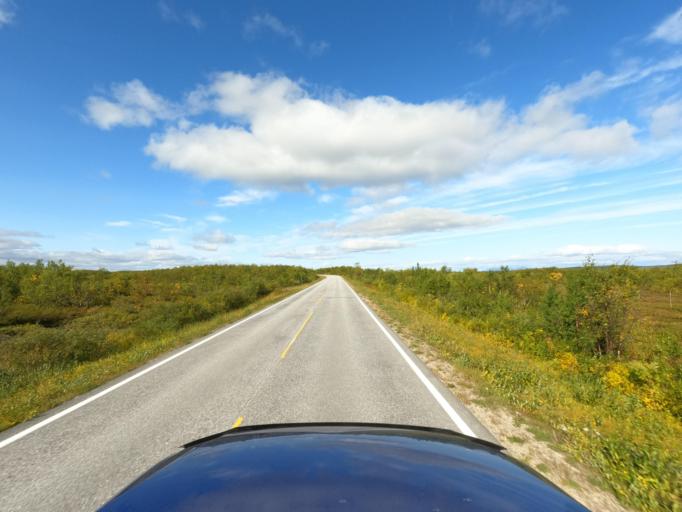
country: NO
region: Finnmark Fylke
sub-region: Karasjok
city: Karasjohka
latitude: 69.6065
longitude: 25.3226
